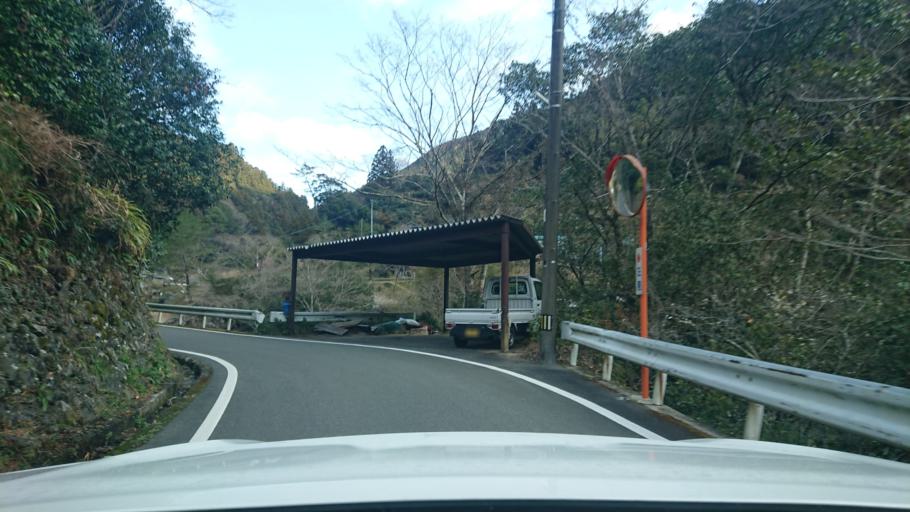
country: JP
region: Tokushima
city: Ishii
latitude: 33.9019
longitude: 134.3953
